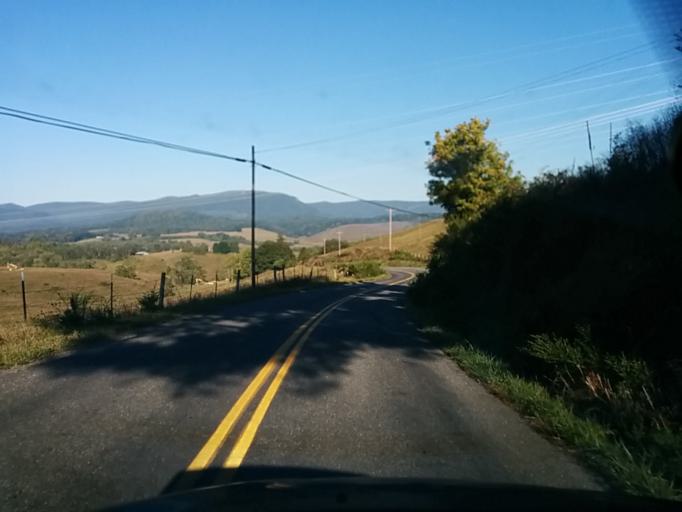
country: US
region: Virginia
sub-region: City of Lexington
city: Lexington
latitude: 37.7466
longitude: -79.5455
